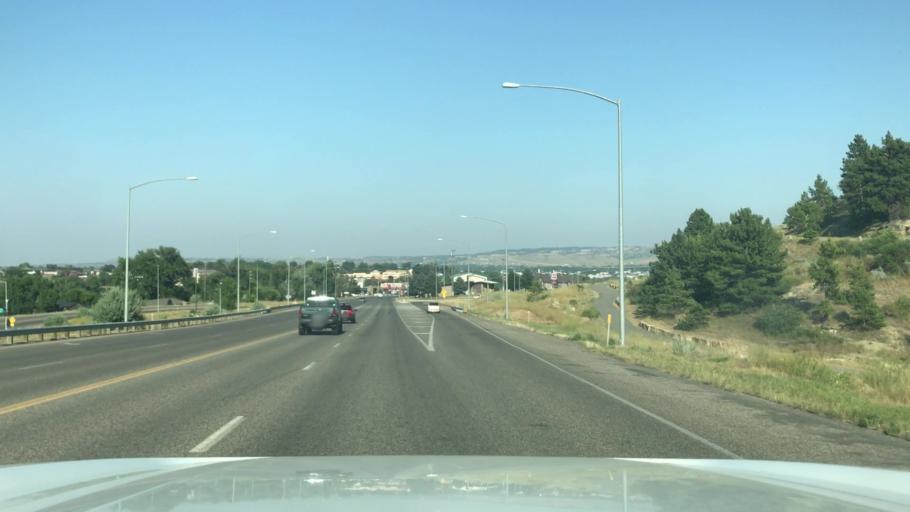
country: US
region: Montana
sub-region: Yellowstone County
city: Billings
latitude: 45.8026
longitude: -108.4857
